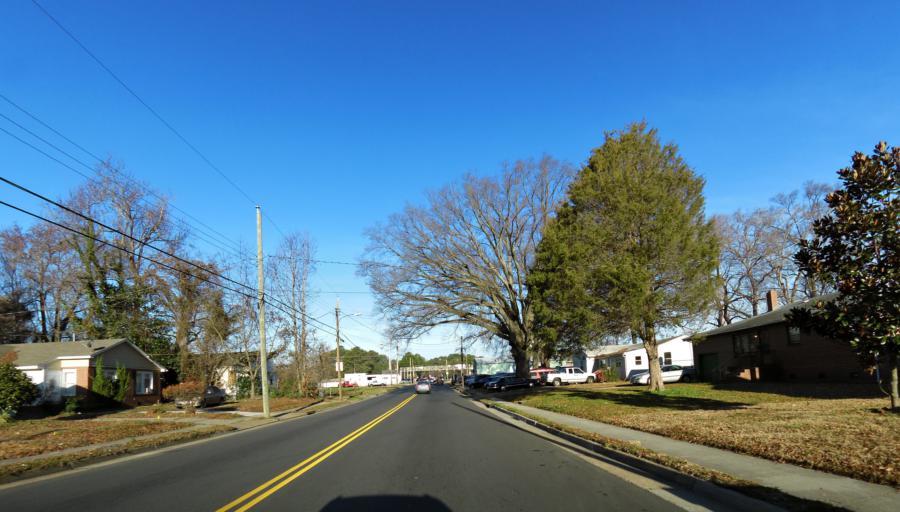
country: US
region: Virginia
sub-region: City of Hampton
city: Hampton
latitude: 37.0115
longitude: -76.3834
